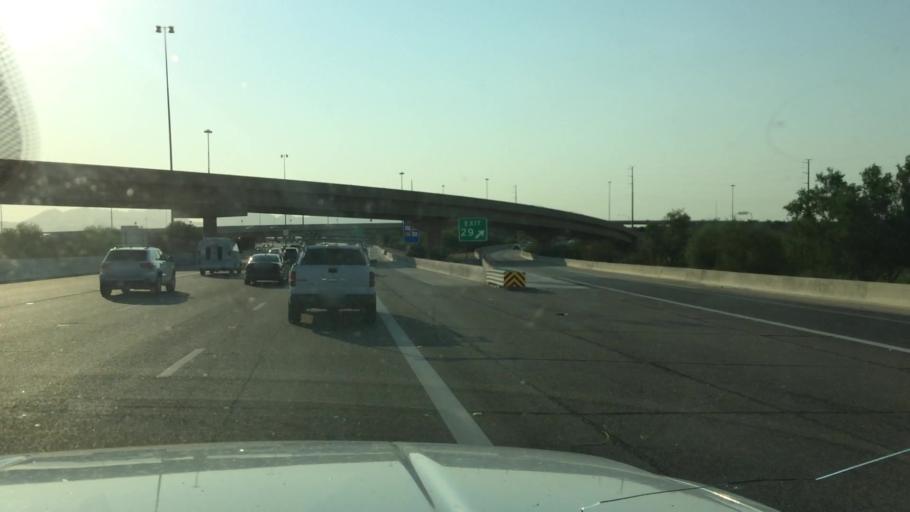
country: US
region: Arizona
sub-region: Maricopa County
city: Paradise Valley
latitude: 33.6712
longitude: -112.0054
